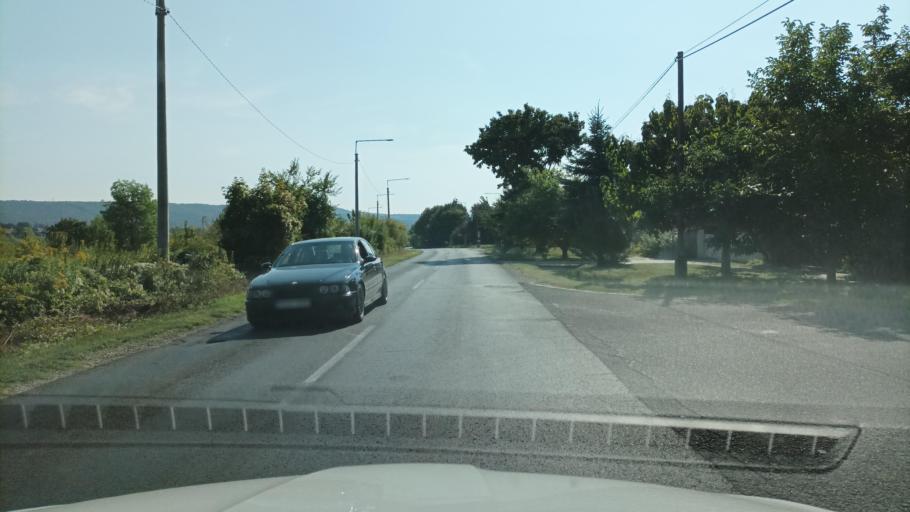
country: HU
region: Pest
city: Godollo
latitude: 47.5854
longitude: 19.3748
